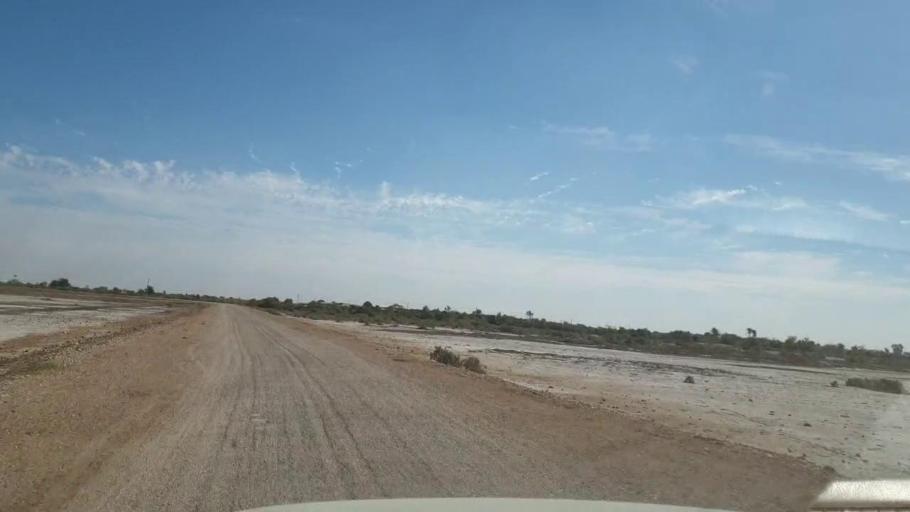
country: PK
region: Sindh
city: Pithoro
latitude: 25.5825
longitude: 69.2884
